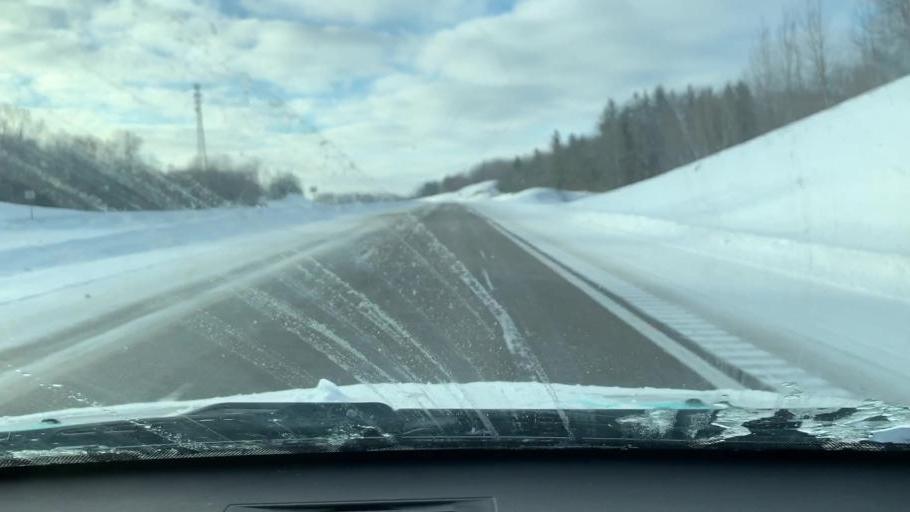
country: US
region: Michigan
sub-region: Wexford County
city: Manton
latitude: 44.3382
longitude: -85.4061
